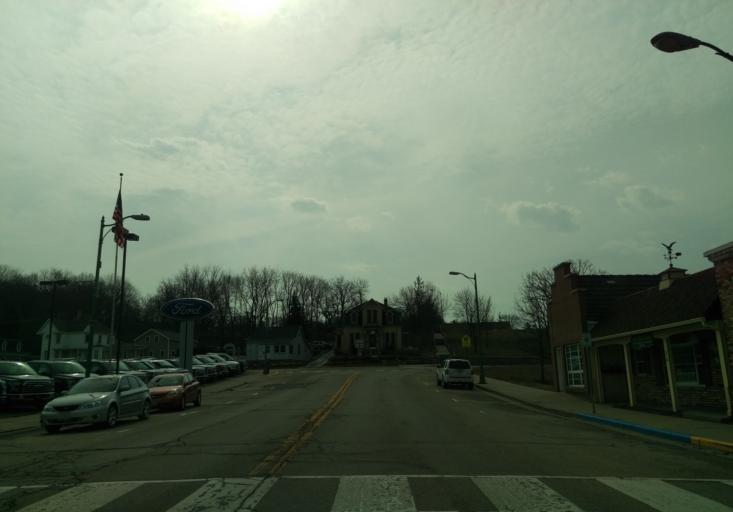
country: US
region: Wisconsin
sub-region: Columbia County
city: Lodi
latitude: 43.3125
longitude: -89.5256
